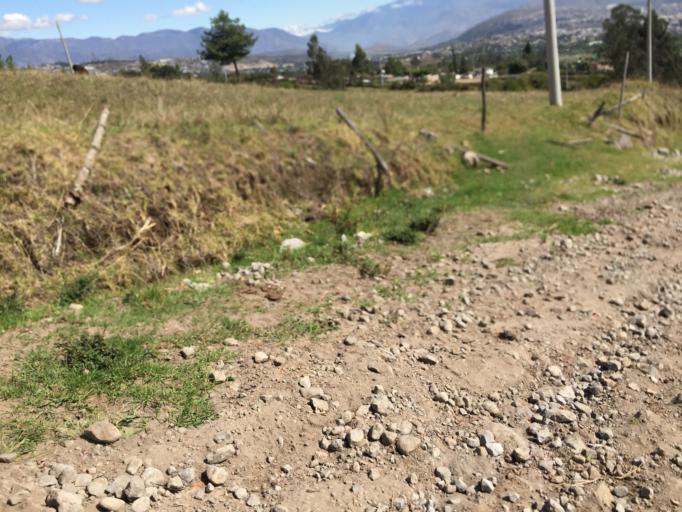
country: EC
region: Imbabura
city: Ibarra
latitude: 0.3096
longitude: -78.1581
